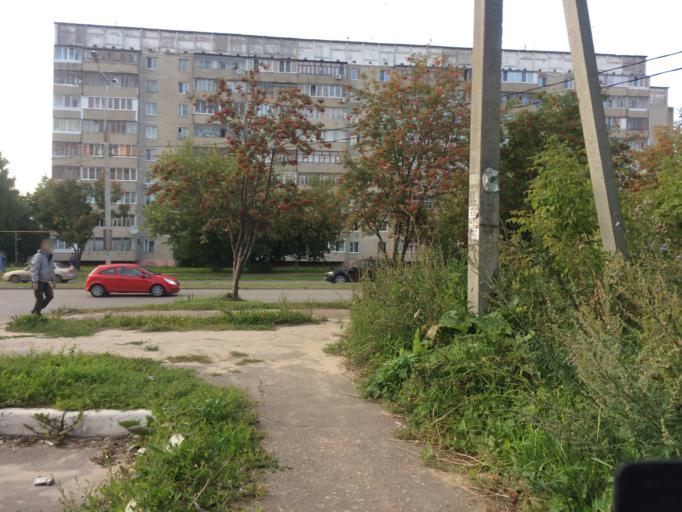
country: RU
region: Mariy-El
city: Yoshkar-Ola
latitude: 56.6414
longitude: 47.8479
